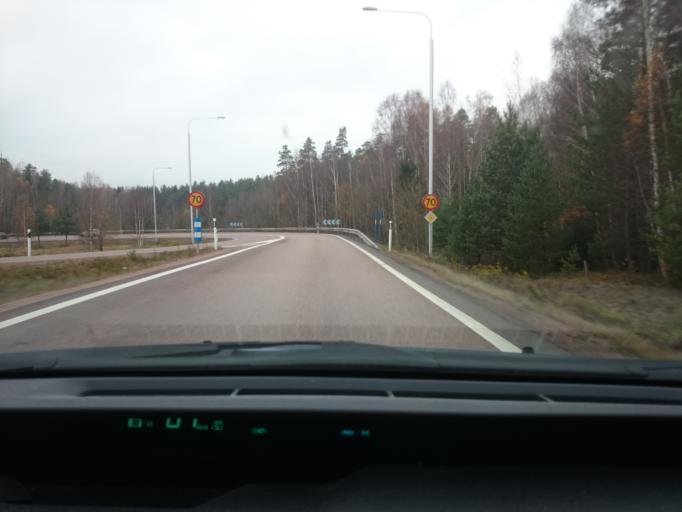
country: SE
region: Dalarna
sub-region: Avesta Kommun
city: Avesta
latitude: 60.1526
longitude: 16.2056
